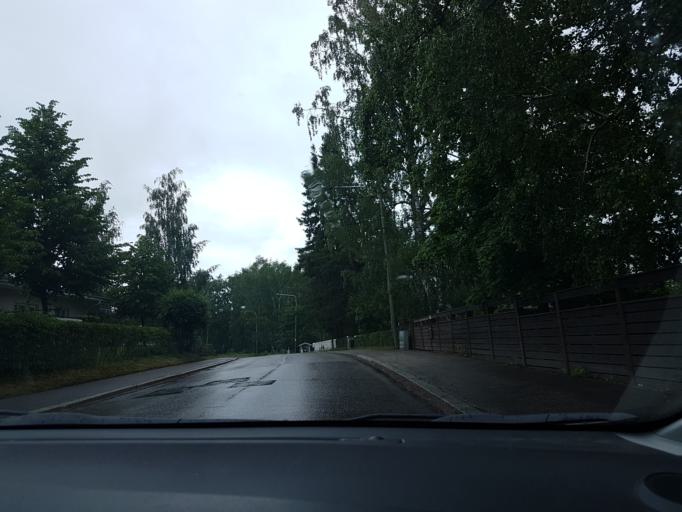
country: FI
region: Uusimaa
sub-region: Helsinki
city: Vantaa
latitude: 60.2301
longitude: 25.0998
